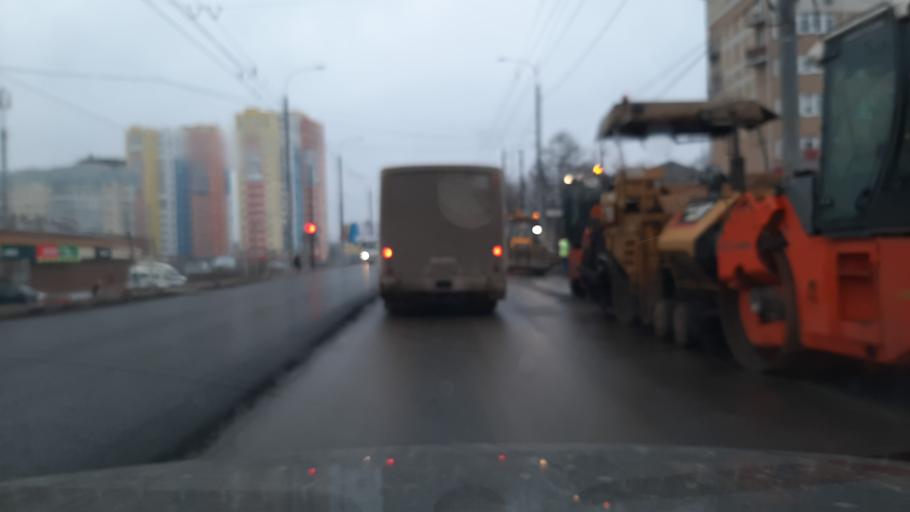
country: RU
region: Ivanovo
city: Kokhma
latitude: 56.9409
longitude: 41.0622
